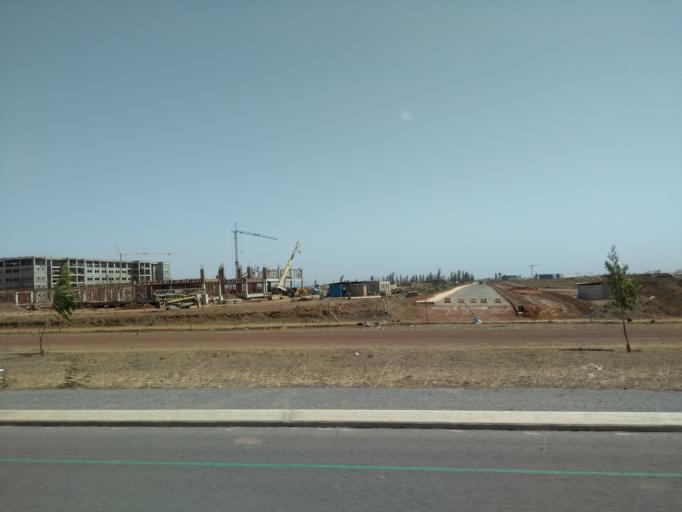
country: SN
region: Thies
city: Thies
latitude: 14.7348
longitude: -17.2003
